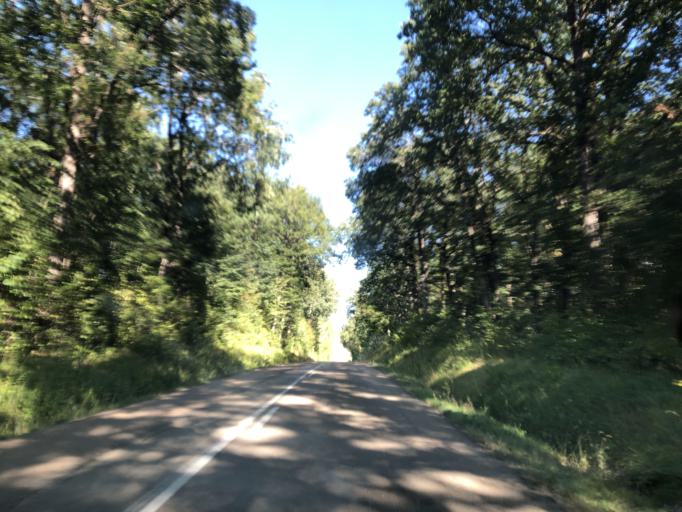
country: FR
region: Bourgogne
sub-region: Departement de l'Yonne
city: Seignelay
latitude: 47.8997
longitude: 3.5741
